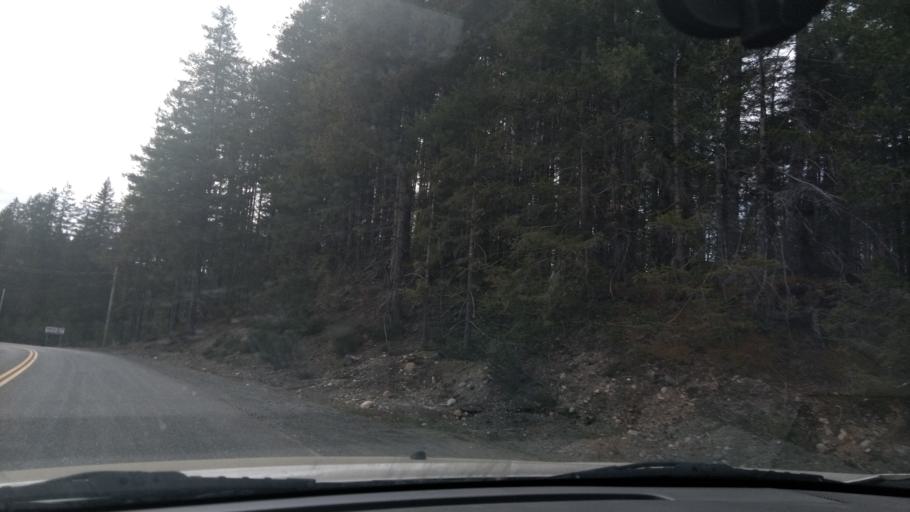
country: CA
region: British Columbia
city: Campbell River
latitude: 50.0032
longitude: -125.3697
